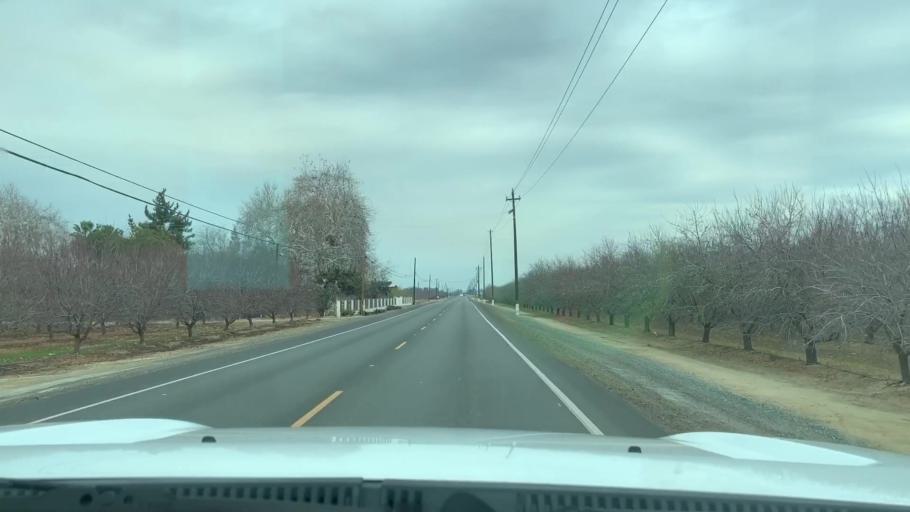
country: US
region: California
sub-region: Kern County
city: Shafter
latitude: 35.4024
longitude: -119.2520
